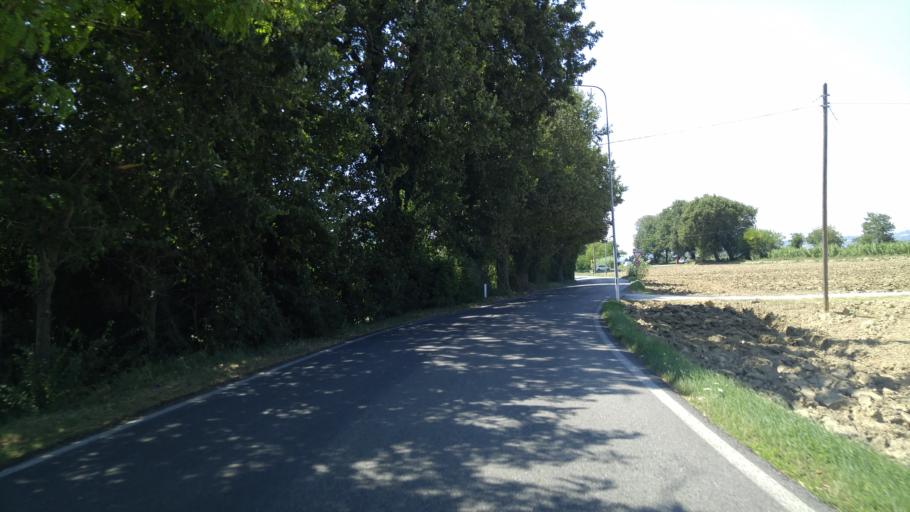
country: IT
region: The Marches
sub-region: Provincia di Pesaro e Urbino
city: Bellocchi
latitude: 43.7972
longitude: 12.9860
